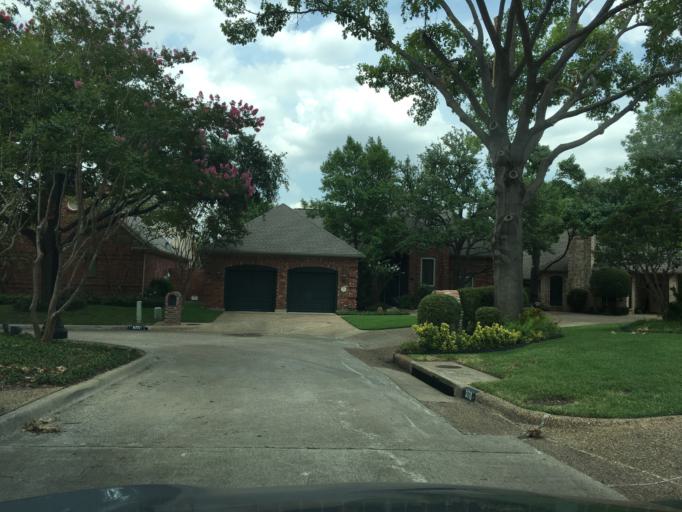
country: US
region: Texas
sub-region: Dallas County
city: Addison
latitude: 32.9479
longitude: -96.8150
